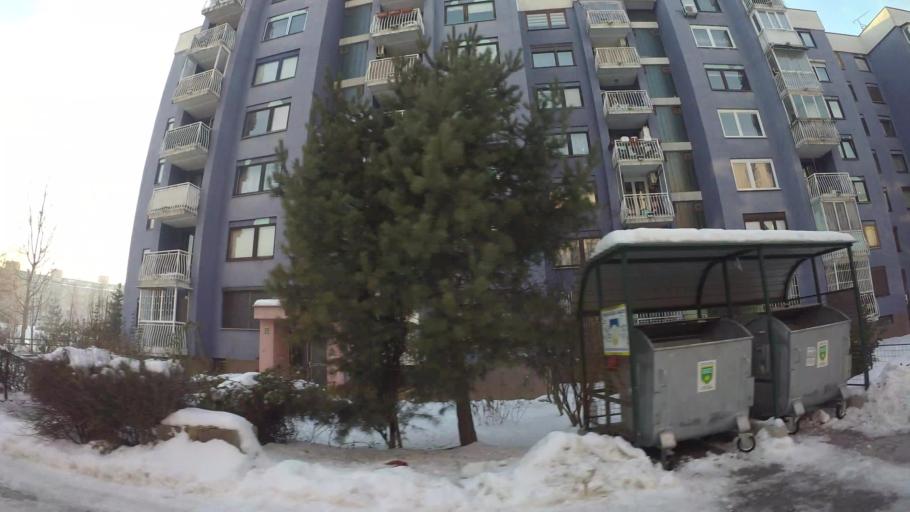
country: BA
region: Federation of Bosnia and Herzegovina
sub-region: Kanton Sarajevo
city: Sarajevo
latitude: 43.8373
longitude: 18.3442
